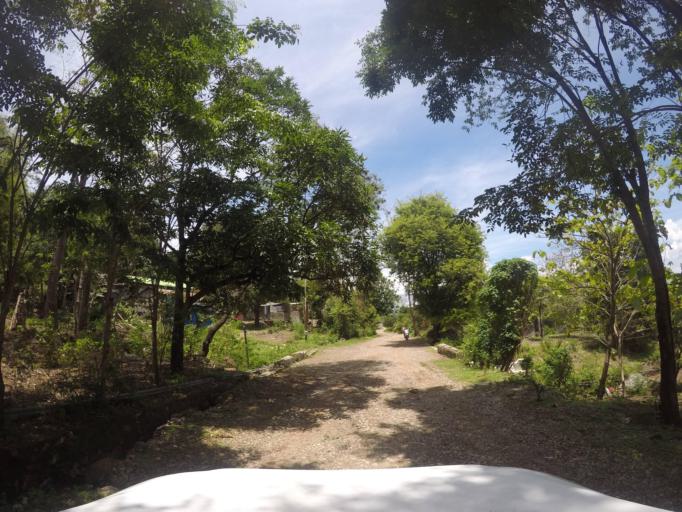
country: TL
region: Bobonaro
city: Maliana
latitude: -8.9962
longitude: 125.2199
